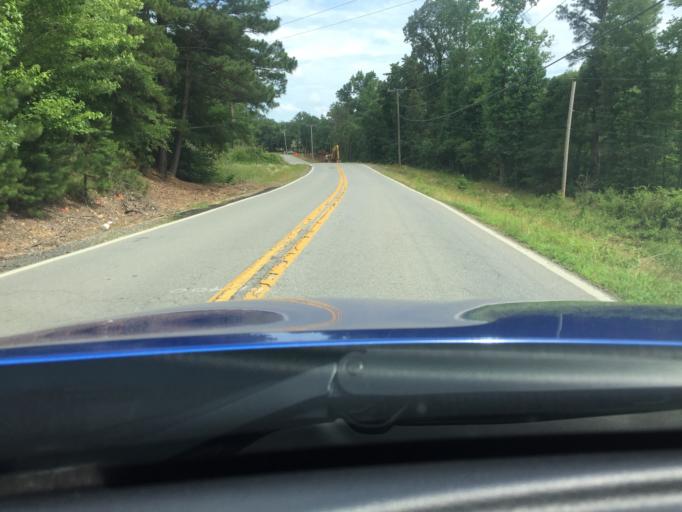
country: US
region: Arkansas
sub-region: Pulaski County
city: Maumelle
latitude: 34.8104
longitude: -92.4426
